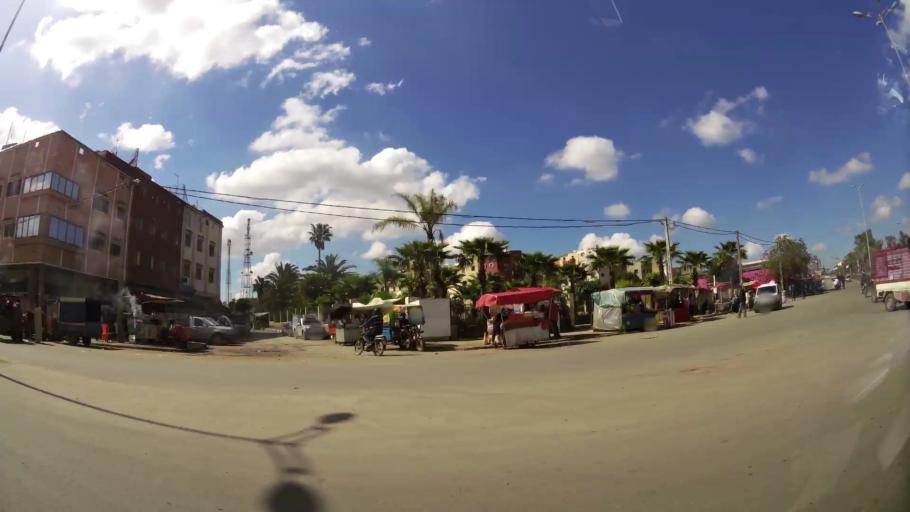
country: MA
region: Grand Casablanca
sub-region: Mediouna
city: Mediouna
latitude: 33.4538
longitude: -7.5187
